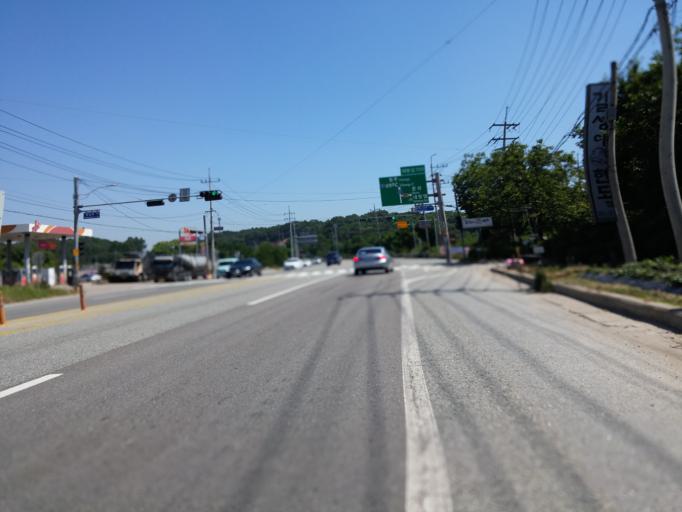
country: KR
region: Daejeon
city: Sintansin
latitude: 36.4718
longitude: 127.4252
